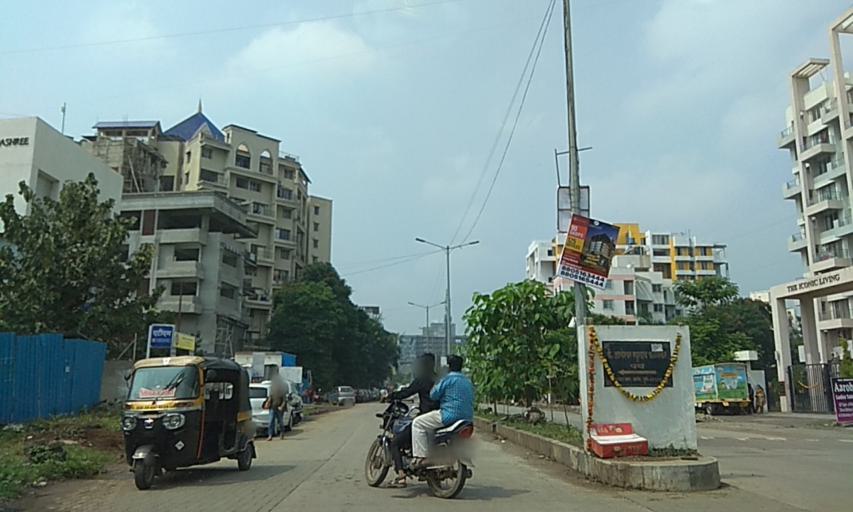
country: IN
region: Maharashtra
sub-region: Pune Division
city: Pimpri
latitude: 18.5583
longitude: 73.7751
